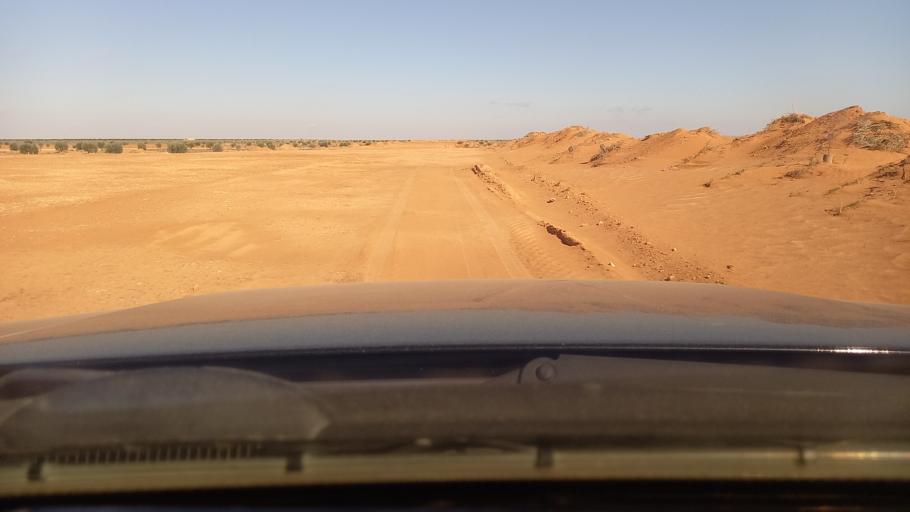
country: TN
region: Madanin
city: Medenine
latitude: 33.1748
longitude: 10.5279
